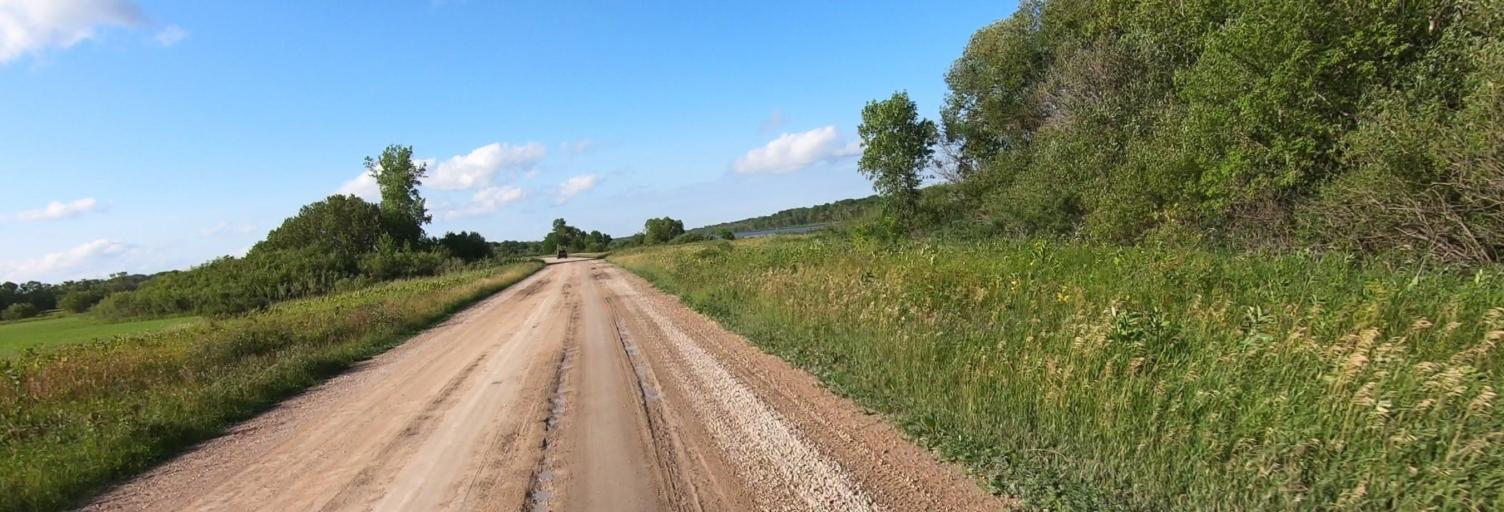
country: CA
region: Manitoba
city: Selkirk
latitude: 50.2557
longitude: -96.8483
